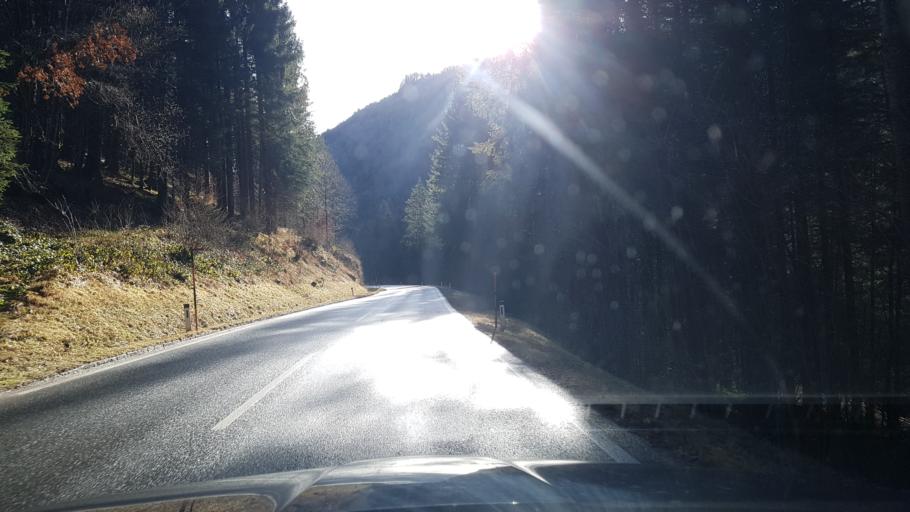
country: AT
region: Salzburg
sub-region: Politischer Bezirk Hallein
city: Krispl
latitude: 47.7358
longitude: 13.1625
